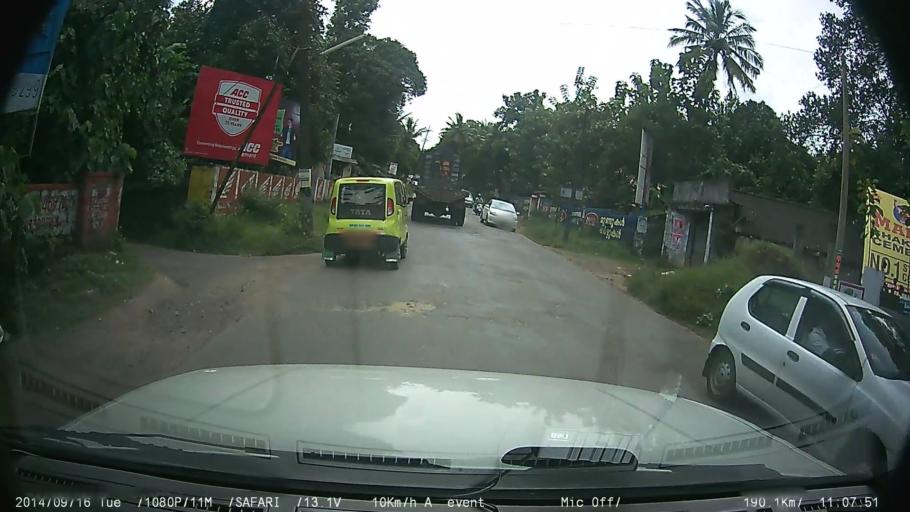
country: IN
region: Kerala
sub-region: Kottayam
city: Kottayam
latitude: 9.5276
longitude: 76.5196
